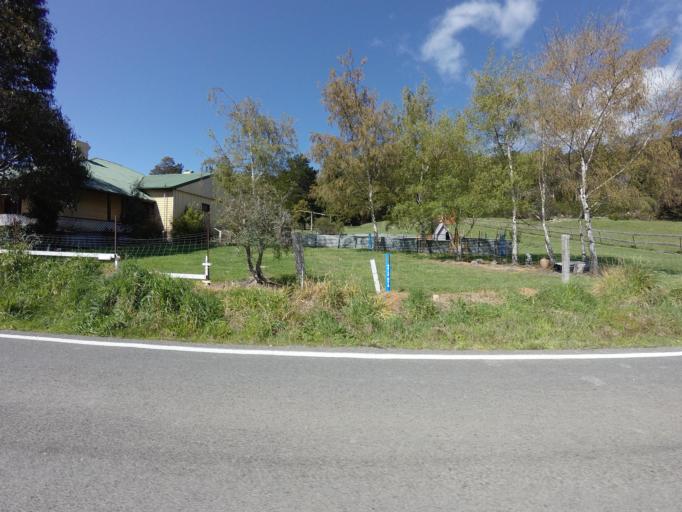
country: AU
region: Tasmania
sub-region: Derwent Valley
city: New Norfolk
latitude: -42.6865
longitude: 146.7183
